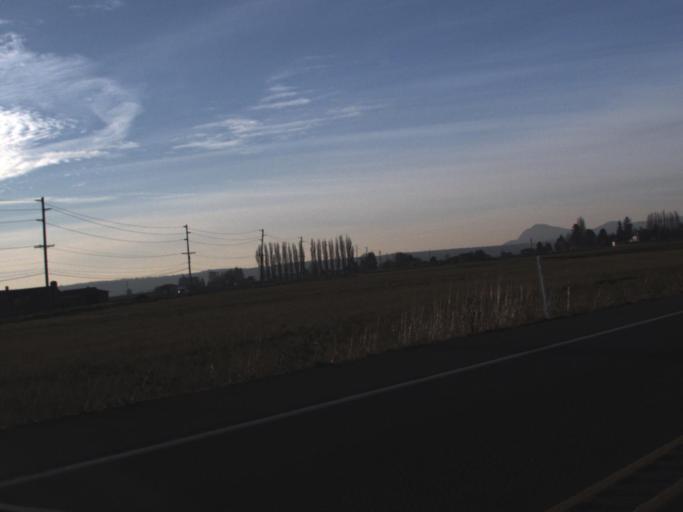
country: US
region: Washington
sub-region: Skagit County
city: Mount Vernon
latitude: 48.4431
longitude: -122.4239
